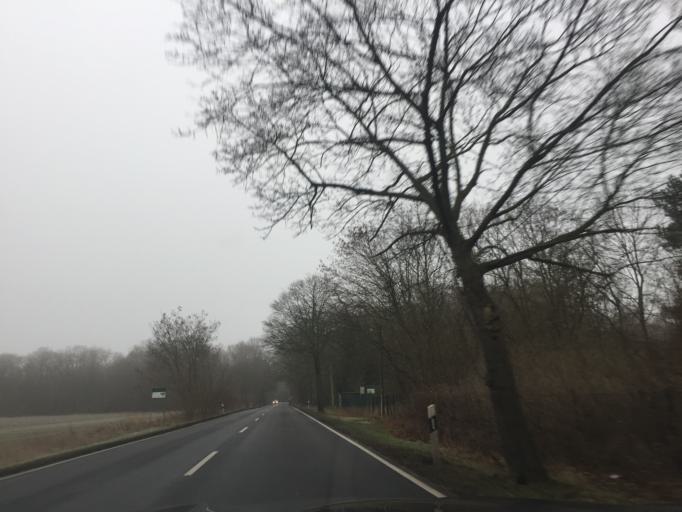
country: DE
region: Brandenburg
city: Hennigsdorf
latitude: 52.6362
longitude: 13.1478
